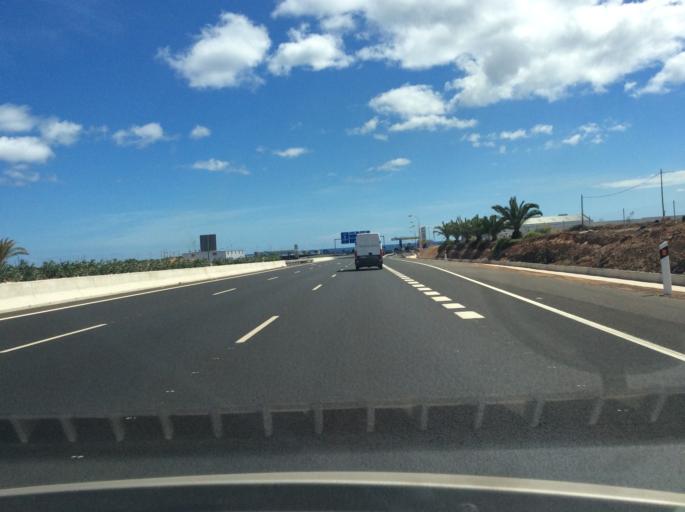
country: ES
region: Canary Islands
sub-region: Provincia de Las Palmas
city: Arrecife
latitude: 28.9805
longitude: -13.5390
